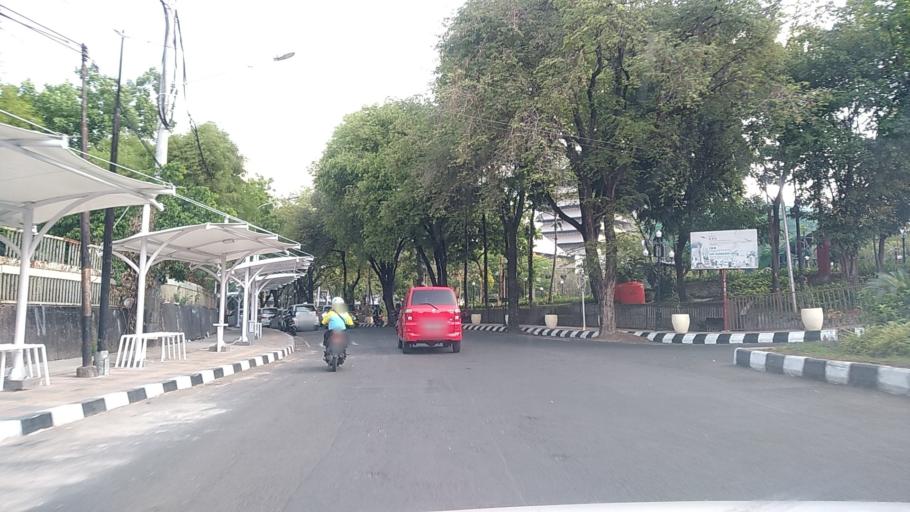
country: ID
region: Central Java
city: Semarang
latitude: -6.9915
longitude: 110.4200
